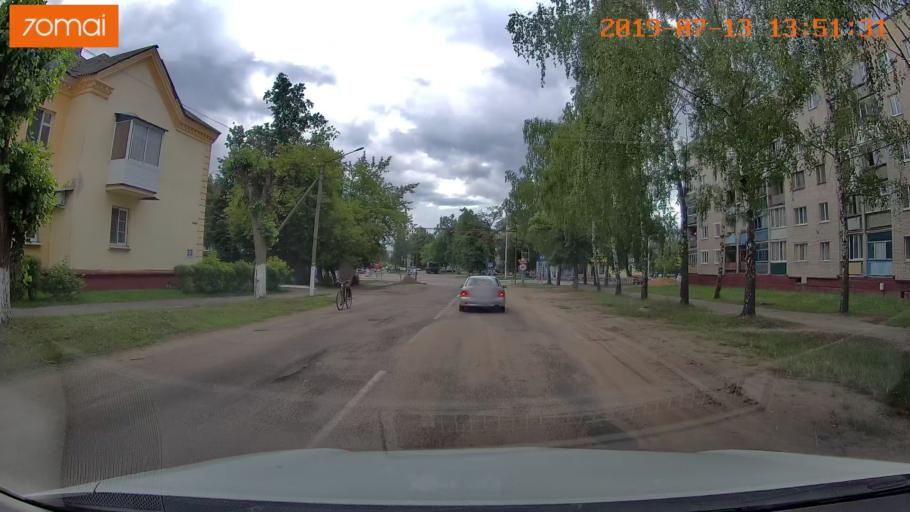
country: BY
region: Mogilev
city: Asipovichy
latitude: 53.2957
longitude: 28.6349
